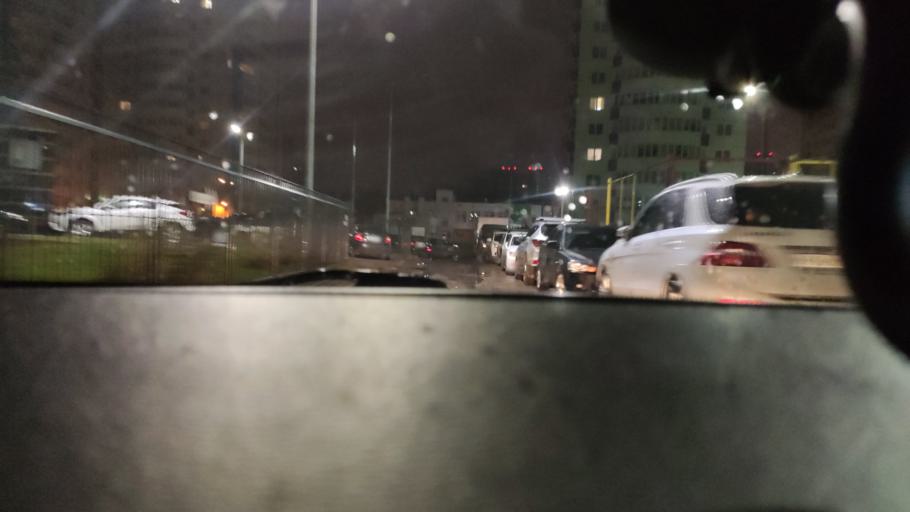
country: RU
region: Perm
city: Perm
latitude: 57.9968
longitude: 56.2683
